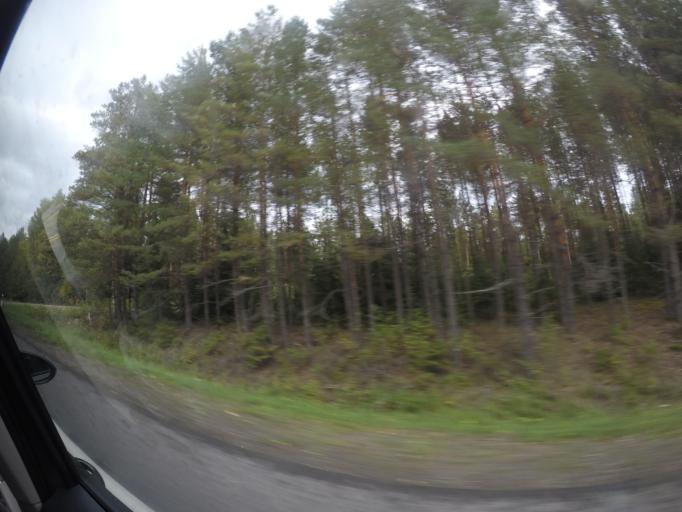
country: FI
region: Haeme
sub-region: Haemeenlinna
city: Parola
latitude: 61.1619
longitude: 24.4110
